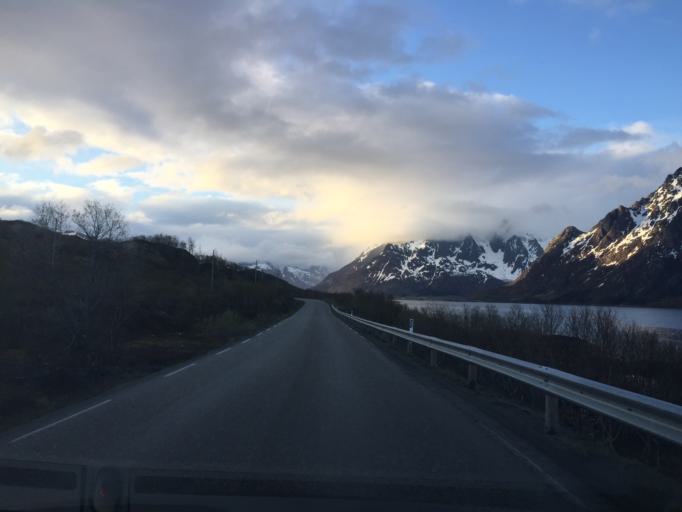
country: NO
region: Nordland
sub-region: Vagan
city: Svolvaer
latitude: 68.2880
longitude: 14.6947
